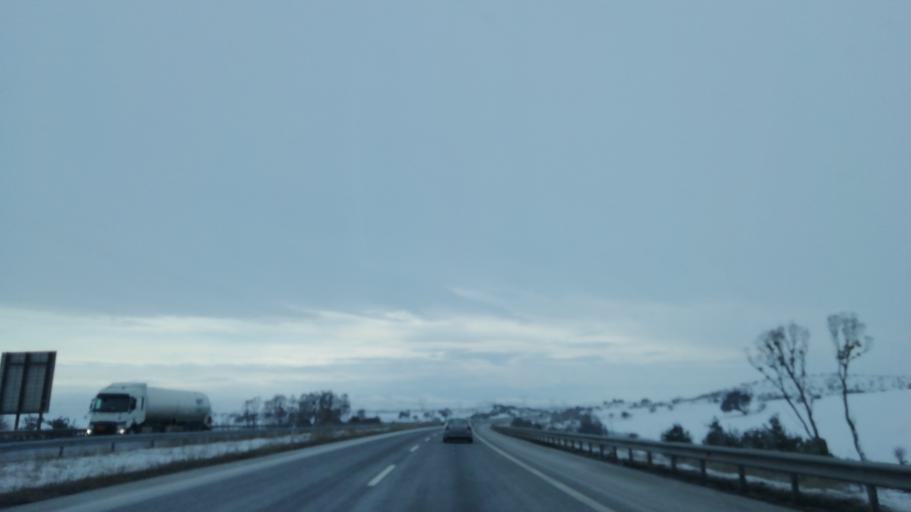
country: TR
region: Bolu
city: Gerede
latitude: 40.7917
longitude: 32.2311
